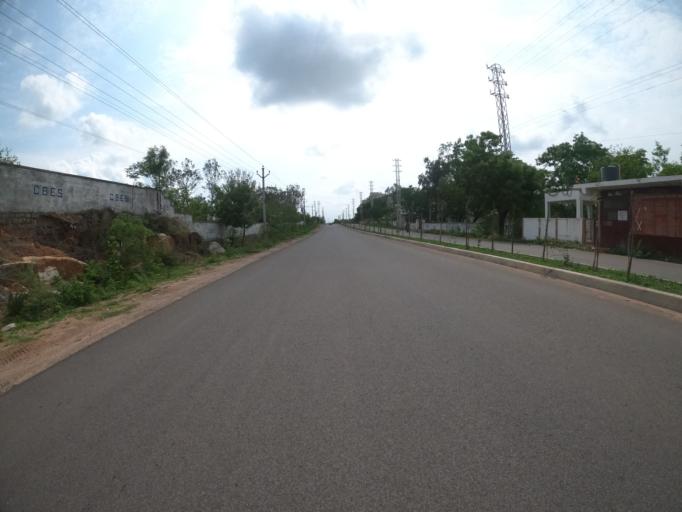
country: IN
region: Telangana
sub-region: Medak
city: Serilingampalle
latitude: 17.3955
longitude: 78.3150
